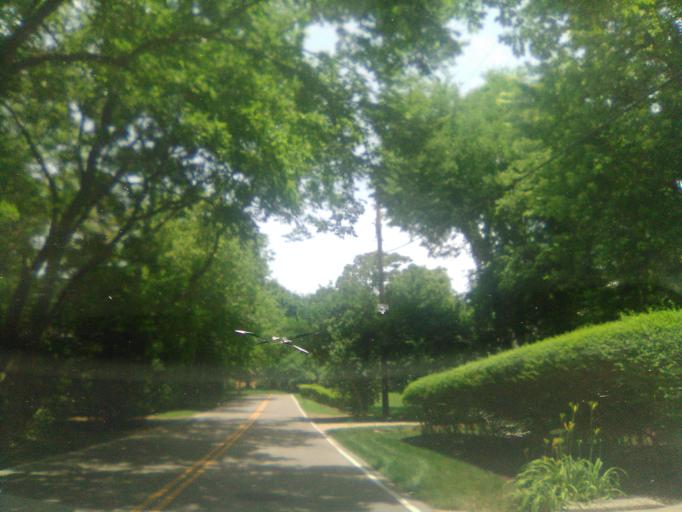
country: US
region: Tennessee
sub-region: Davidson County
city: Belle Meade
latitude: 36.0982
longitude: -86.8521
